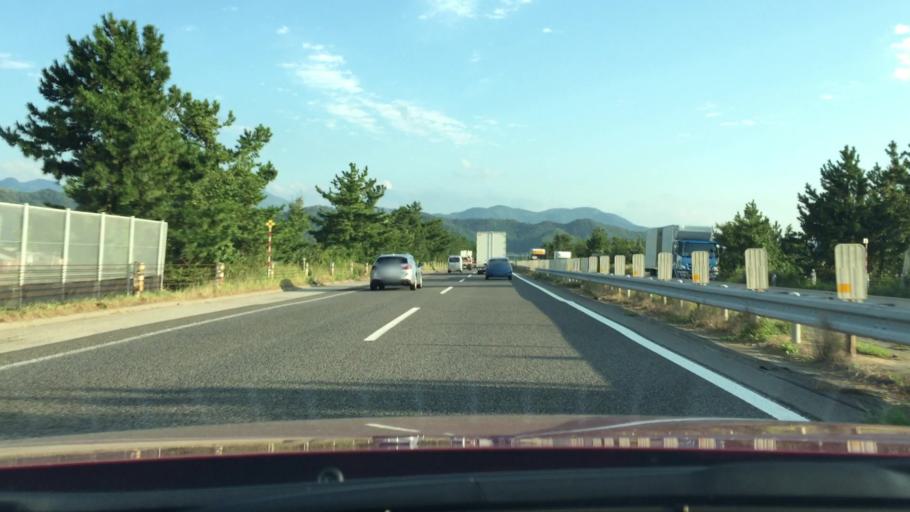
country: JP
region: Shiga Prefecture
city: Nagahama
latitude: 35.3718
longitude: 136.3040
